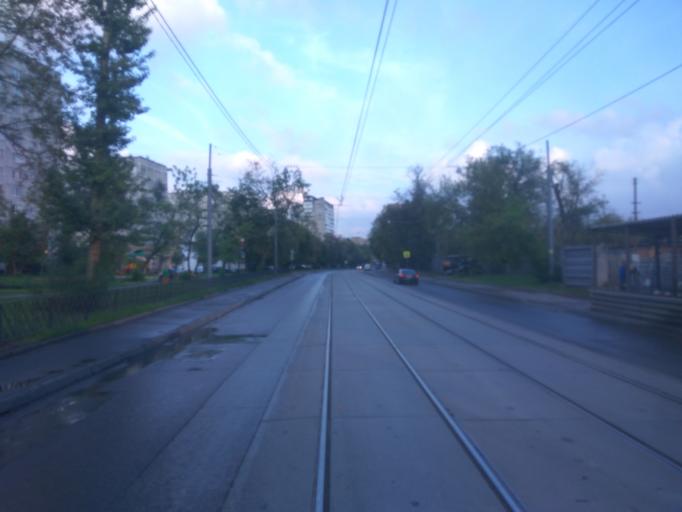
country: RU
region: Moskovskaya
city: Bogorodskoye
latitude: 55.8117
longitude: 37.7000
